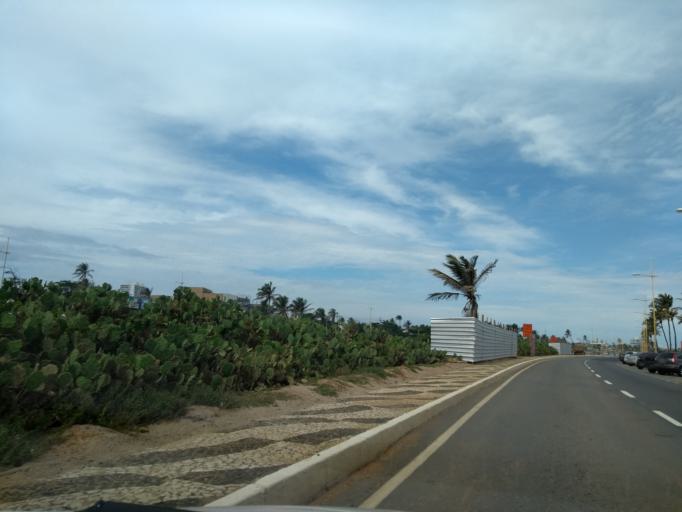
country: BR
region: Bahia
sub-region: Lauro De Freitas
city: Lauro de Freitas
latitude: -12.9580
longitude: -38.3913
